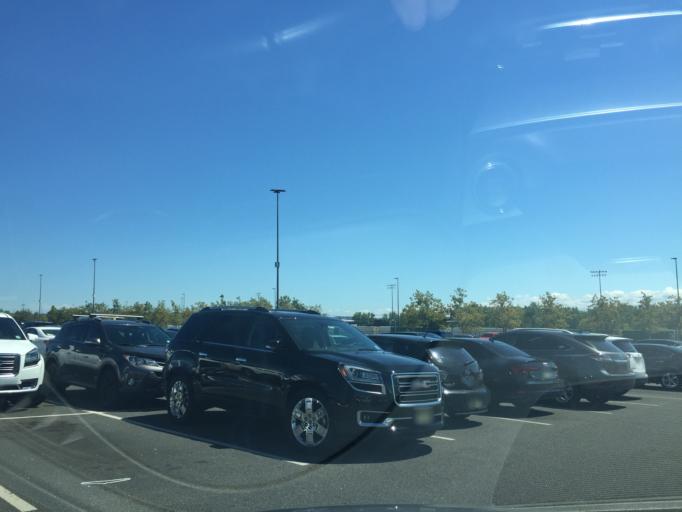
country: US
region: New Jersey
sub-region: Union County
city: Elizabeth
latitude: 40.6589
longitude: -74.1724
